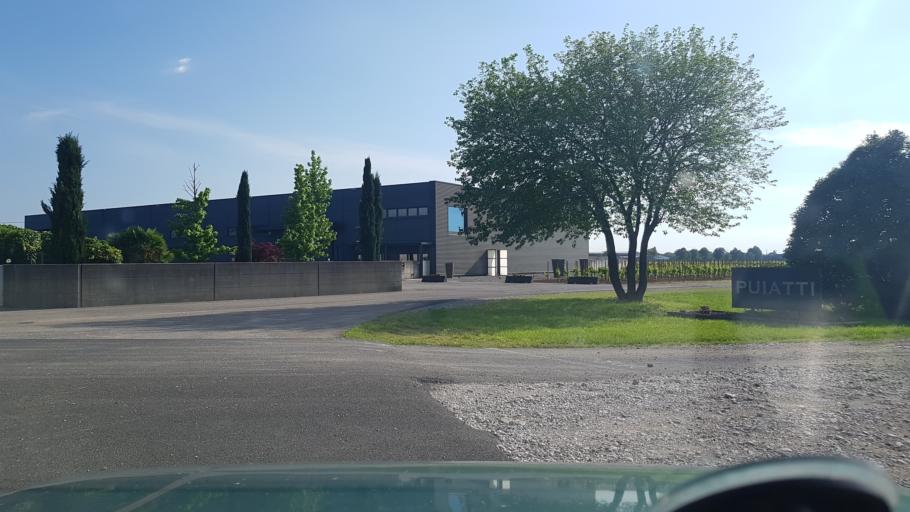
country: IT
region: Friuli Venezia Giulia
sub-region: Provincia di Gorizia
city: Mariano del Friuli
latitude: 45.8969
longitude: 13.4641
